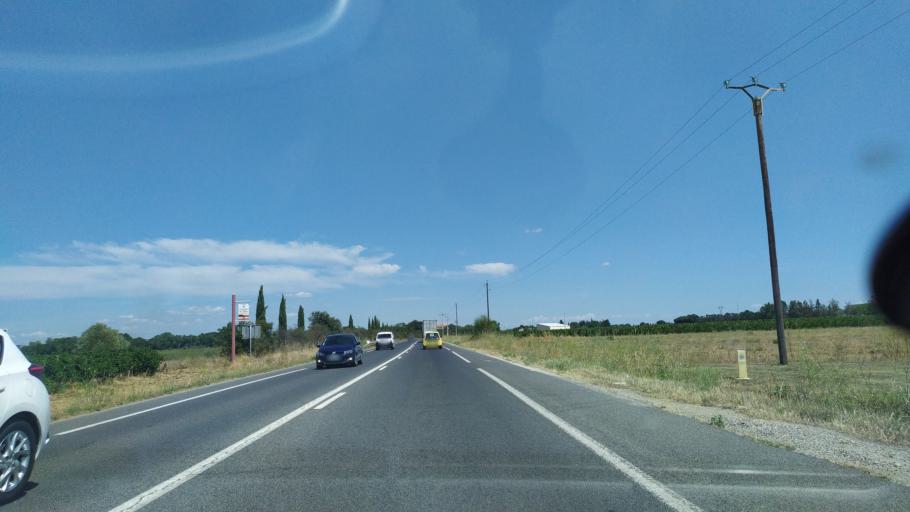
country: FR
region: Languedoc-Roussillon
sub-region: Departement du Gard
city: Aubord
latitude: 43.7617
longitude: 4.3161
